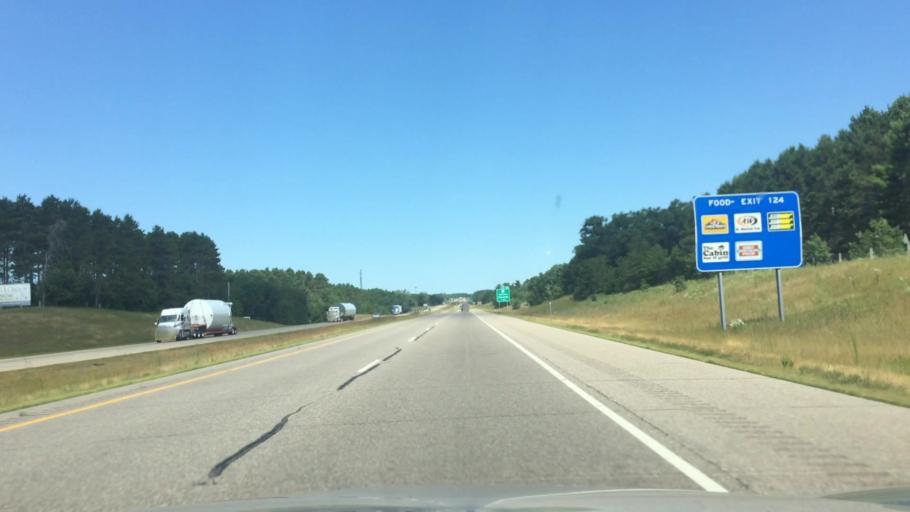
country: US
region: Wisconsin
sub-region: Marquette County
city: Westfield
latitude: 44.0167
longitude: -89.5114
